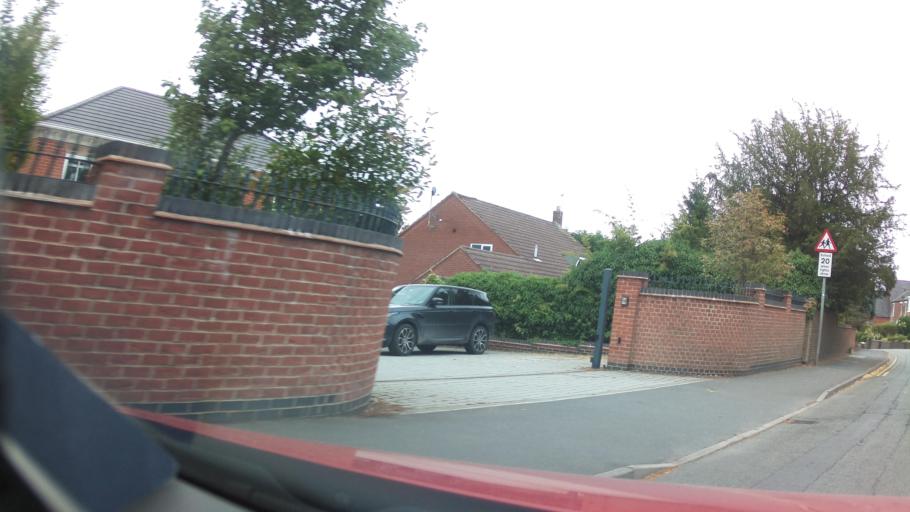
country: GB
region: England
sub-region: Leicestershire
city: Ashby de la Zouch
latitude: 52.7482
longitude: -1.4795
